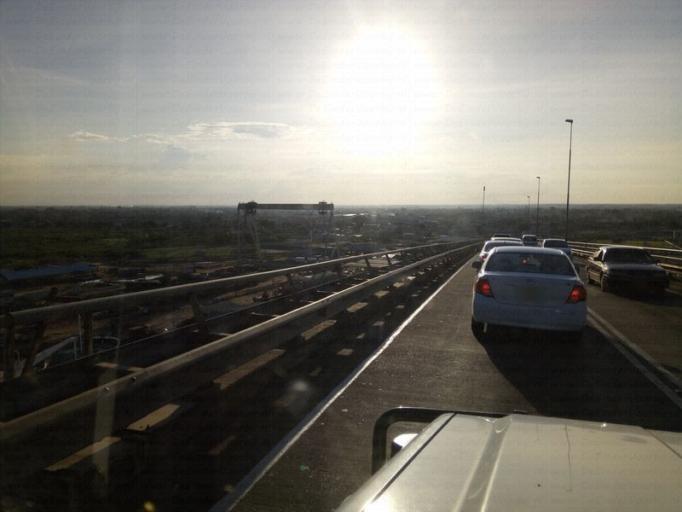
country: SR
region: Paramaribo
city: Paramaribo
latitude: 5.8054
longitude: -55.1653
